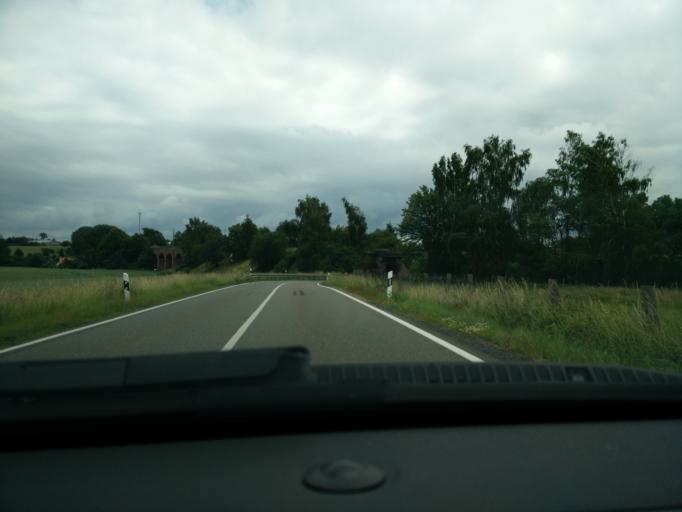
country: DE
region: Saxony
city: Geithain
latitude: 51.0634
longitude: 12.6718
